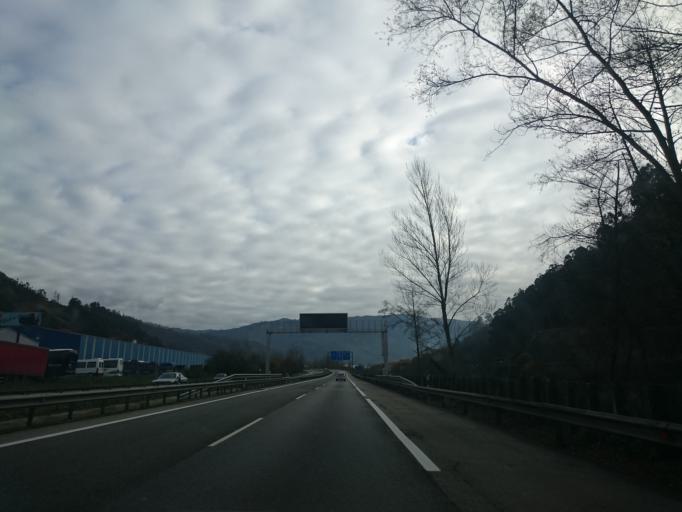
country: ES
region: Asturias
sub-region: Province of Asturias
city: Mieres
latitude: 43.2672
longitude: -5.7984
